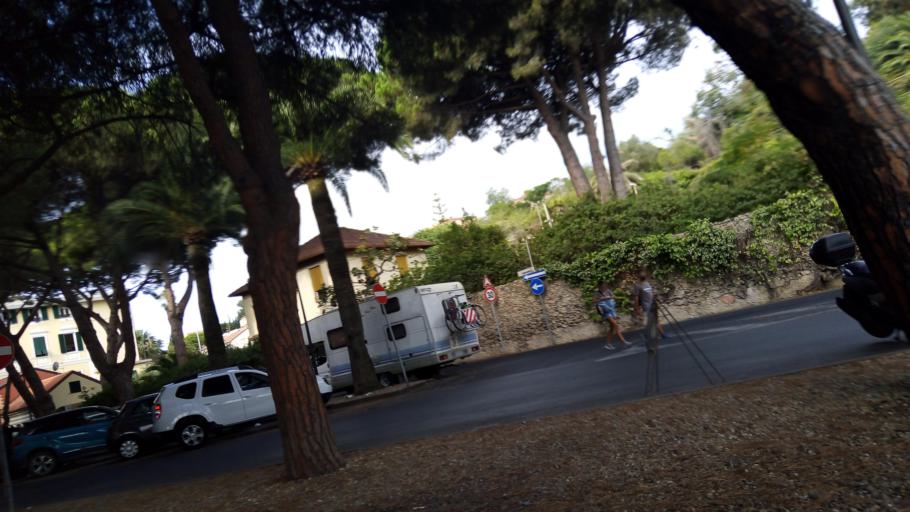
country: IT
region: Liguria
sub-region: Provincia di Savona
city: Ceriale
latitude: 44.1000
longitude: 8.2357
